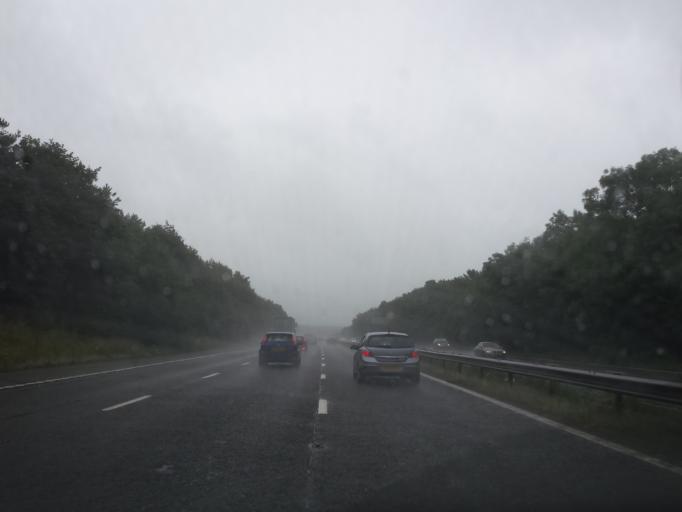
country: GB
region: England
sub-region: Leicestershire
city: Markfield
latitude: 52.6660
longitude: -1.2729
